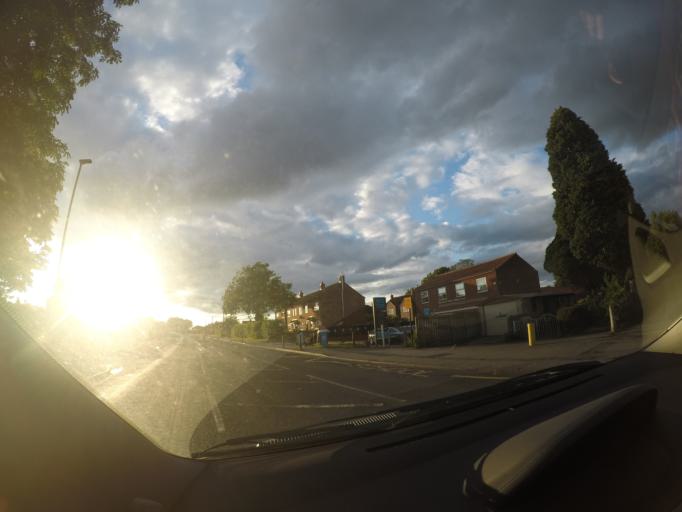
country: GB
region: England
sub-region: North Yorkshire
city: Catterick
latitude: 54.3780
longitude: -1.6322
